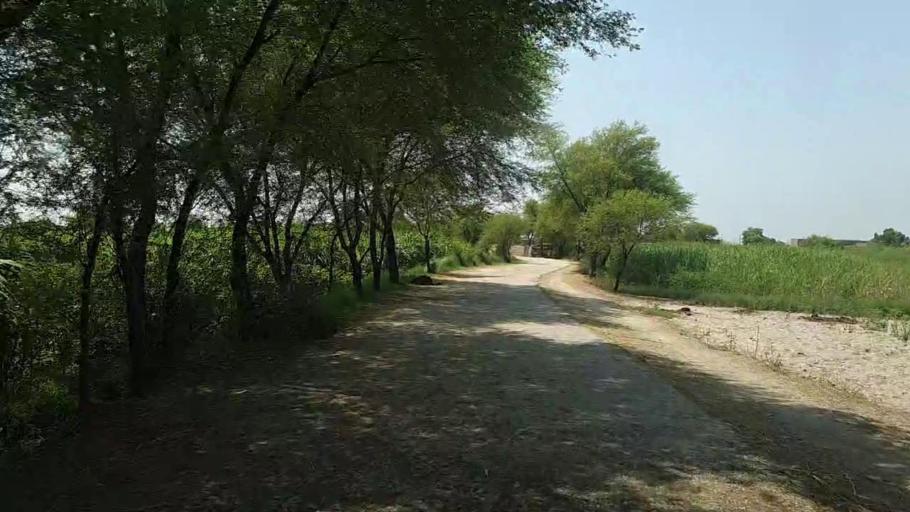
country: PK
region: Sindh
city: Ubauro
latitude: 28.1993
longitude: 69.8028
